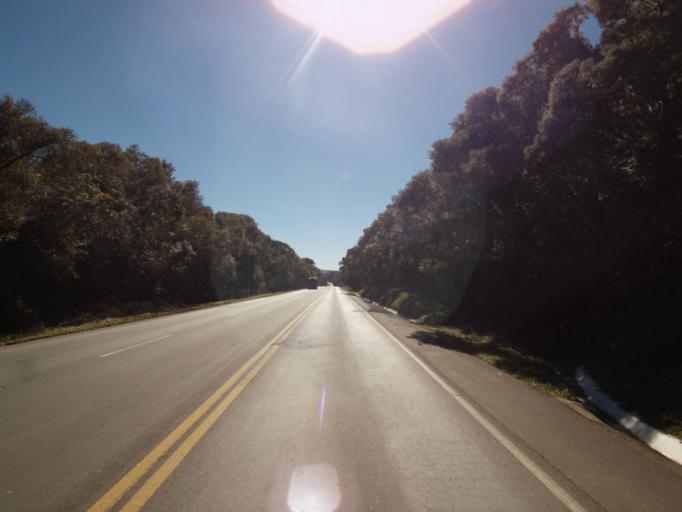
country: BR
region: Santa Catarina
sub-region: Concordia
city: Concordia
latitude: -26.9612
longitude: -51.8550
